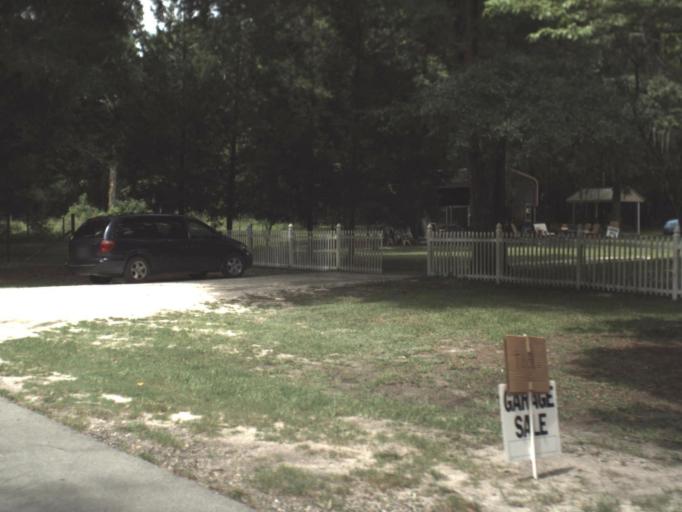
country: US
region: Florida
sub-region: Alachua County
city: High Springs
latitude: 29.8064
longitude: -82.6078
